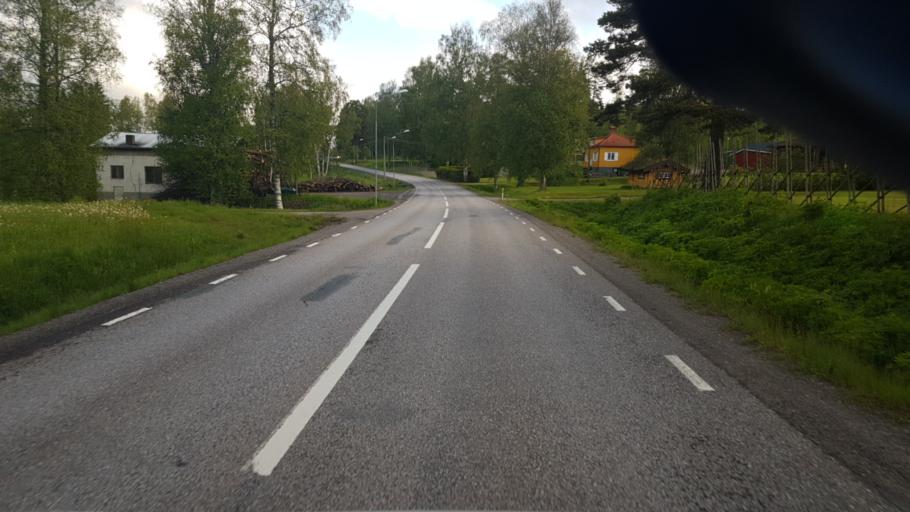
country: SE
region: Vaermland
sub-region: Eda Kommun
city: Amotfors
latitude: 59.6825
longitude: 12.1481
